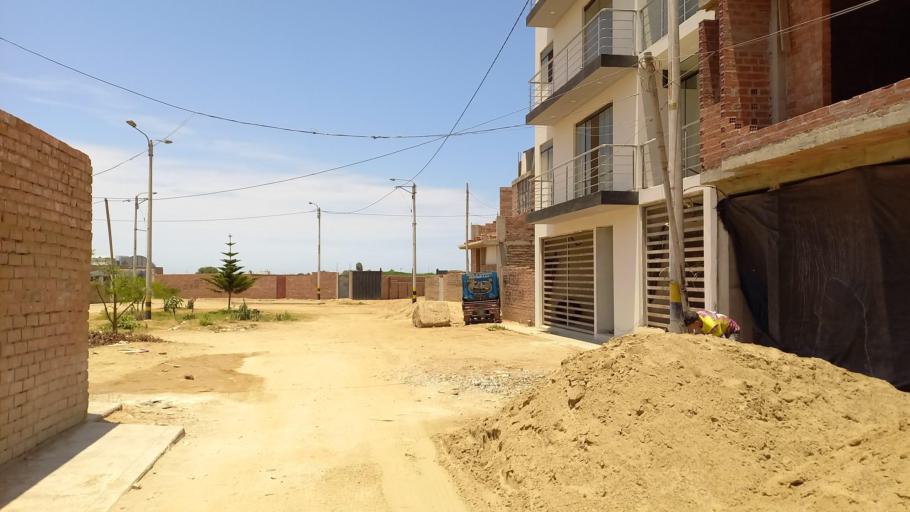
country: PE
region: La Libertad
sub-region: Provincia de Trujillo
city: Trujillo
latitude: -8.1185
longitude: -79.0480
